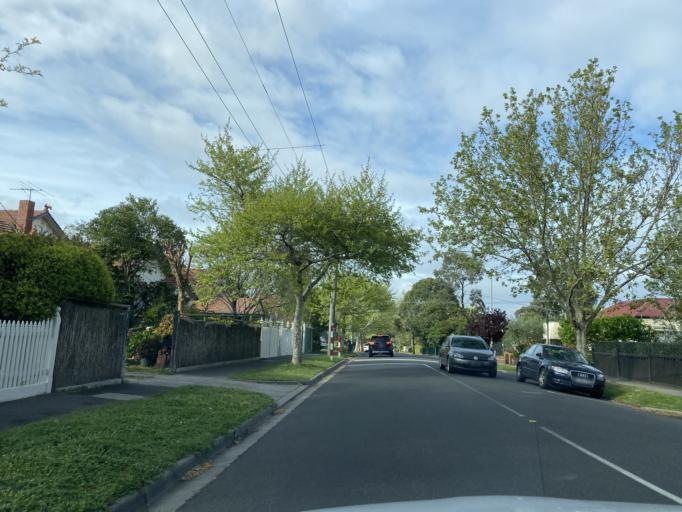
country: AU
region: Victoria
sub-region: Boroondara
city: Canterbury
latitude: -37.8302
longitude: 145.0858
